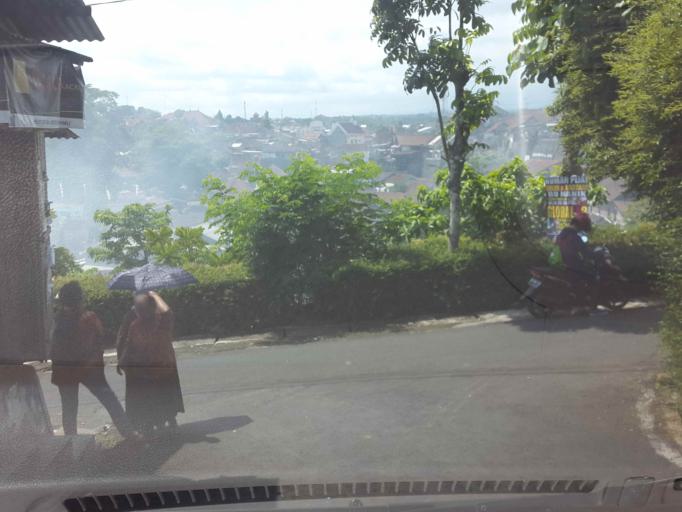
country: ID
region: Central Java
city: Salatiga
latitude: -7.3227
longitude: 110.5071
